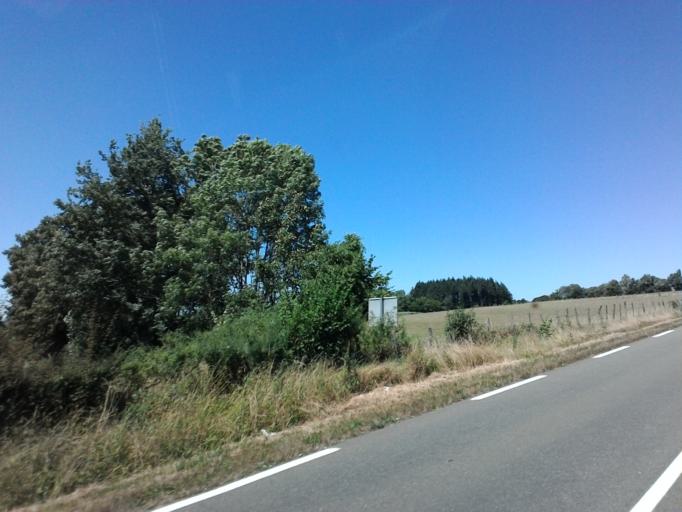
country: FR
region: Franche-Comte
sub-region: Departement du Jura
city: Saint-Amour
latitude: 46.4625
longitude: 5.3575
